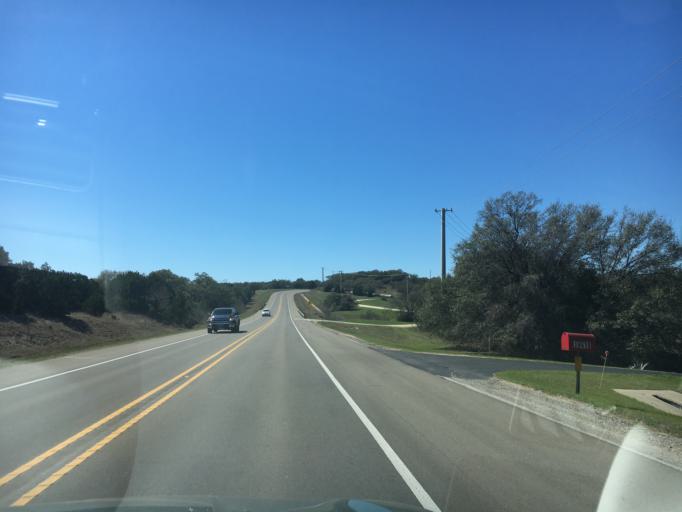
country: US
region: Texas
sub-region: Travis County
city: The Hills
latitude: 30.2868
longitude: -98.0577
